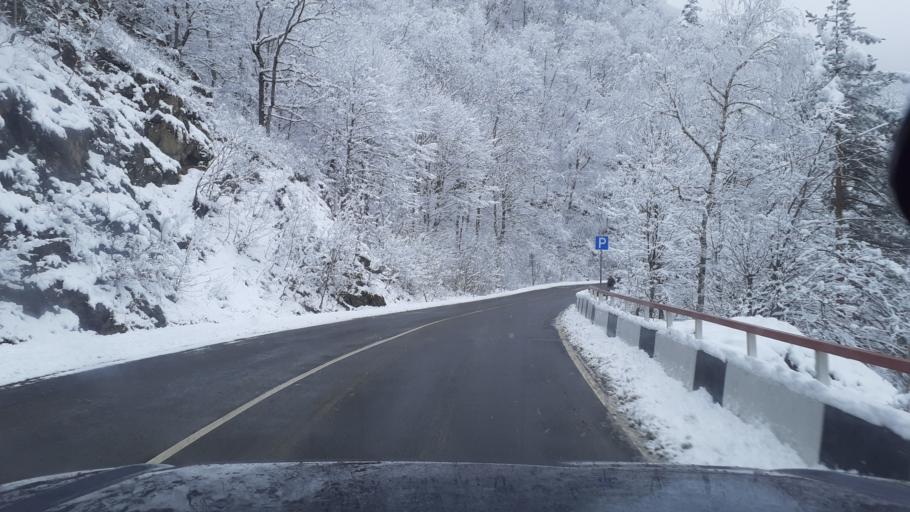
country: RU
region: Adygeya
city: Kamennomostskiy
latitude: 44.1661
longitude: 40.1463
